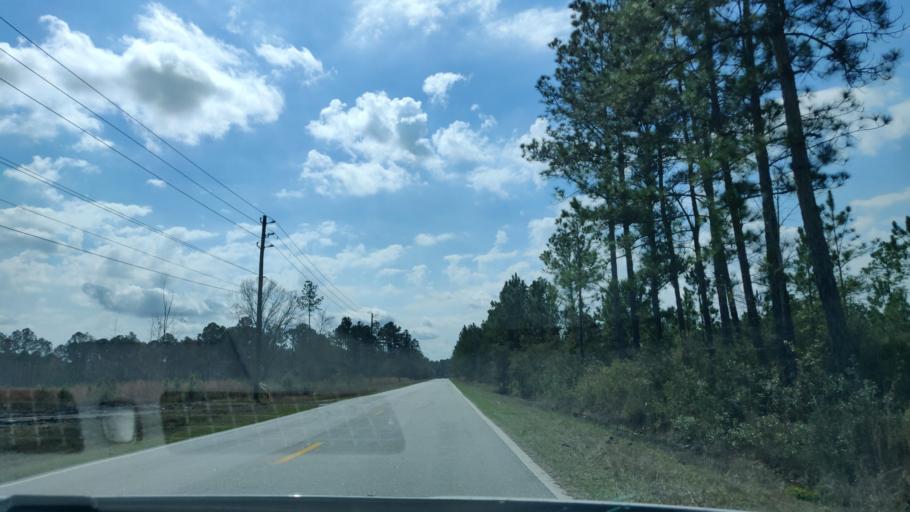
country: US
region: Florida
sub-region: Duval County
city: Baldwin
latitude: 30.2261
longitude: -81.9411
